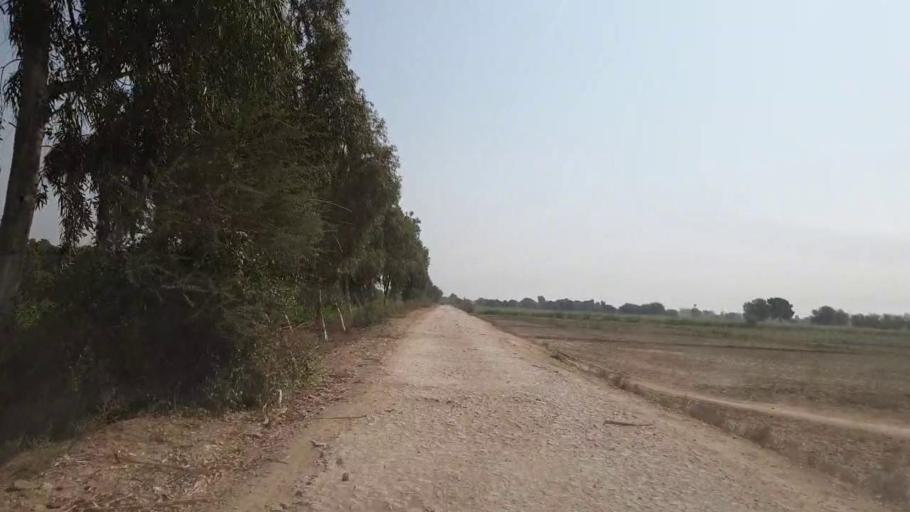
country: PK
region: Sindh
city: Mirpur Khas
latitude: 25.6485
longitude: 69.1506
